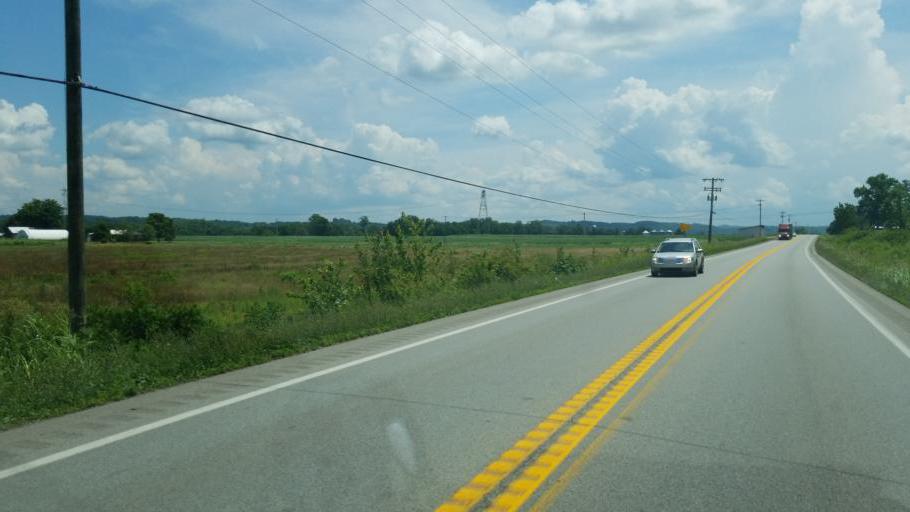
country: US
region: West Virginia
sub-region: Putnam County
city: Buffalo
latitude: 38.7505
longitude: -81.9850
